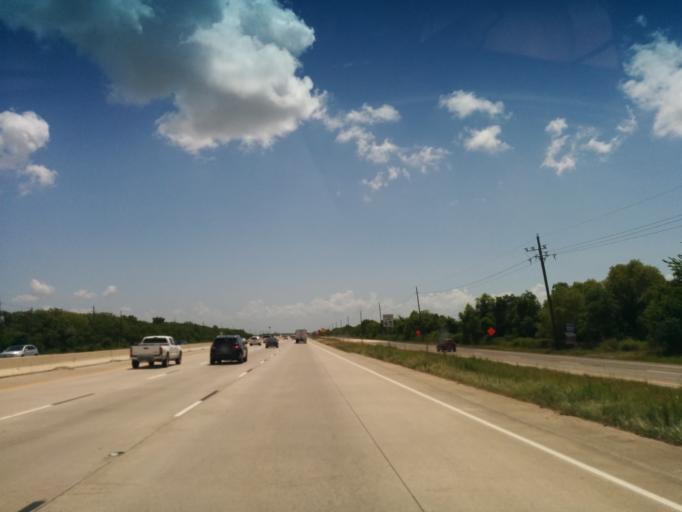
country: US
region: Texas
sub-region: Chambers County
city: Mont Belvieu
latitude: 29.8249
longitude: -94.8580
